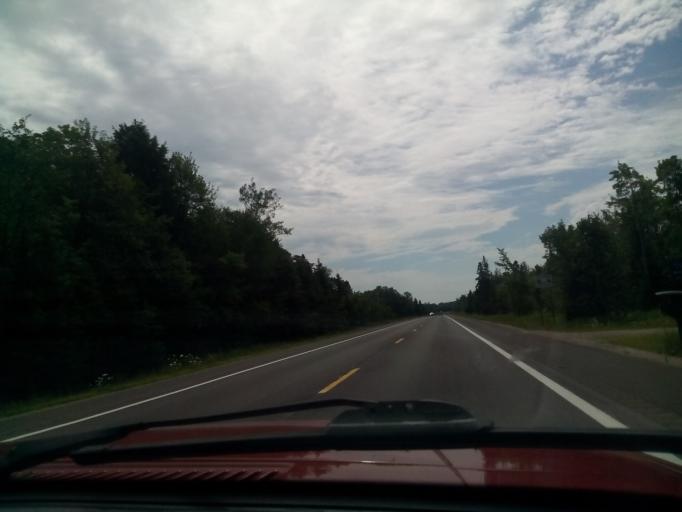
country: US
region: Michigan
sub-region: Schoolcraft County
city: Manistique
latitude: 46.0711
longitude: -85.9584
